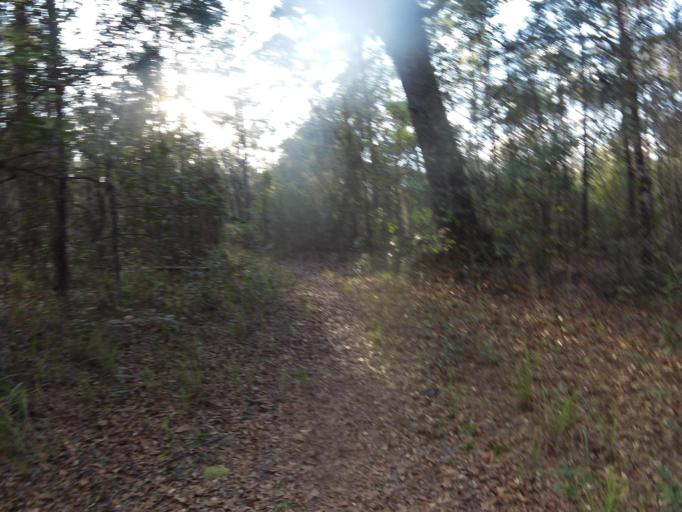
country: US
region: Florida
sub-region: Putnam County
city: Interlachen
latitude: 29.7651
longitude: -81.8442
